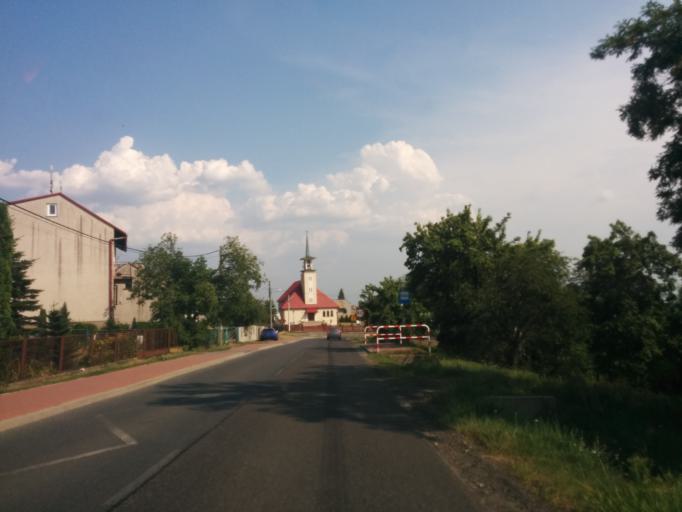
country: PL
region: Silesian Voivodeship
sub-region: Powiat myszkowski
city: Choron
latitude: 50.7054
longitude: 19.2849
